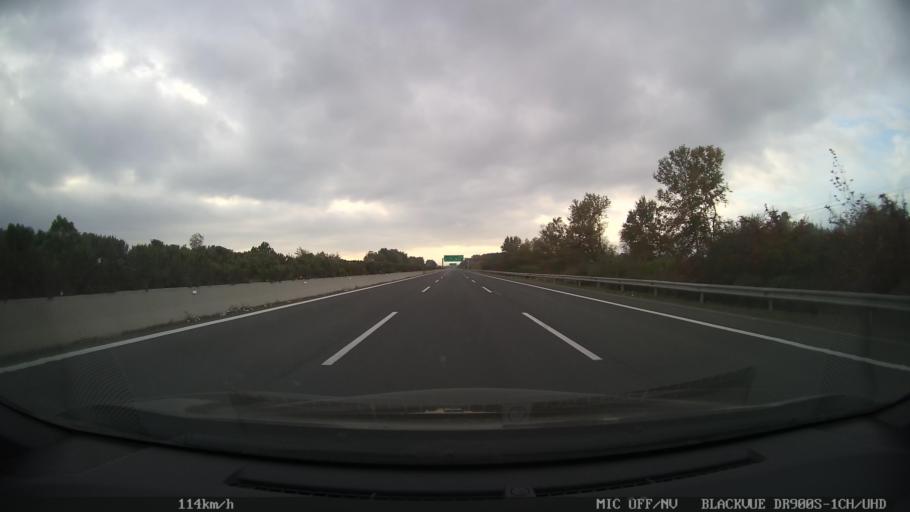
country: GR
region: Central Macedonia
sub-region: Nomos Pierias
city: Nea Efesos
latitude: 40.2093
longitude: 22.5446
